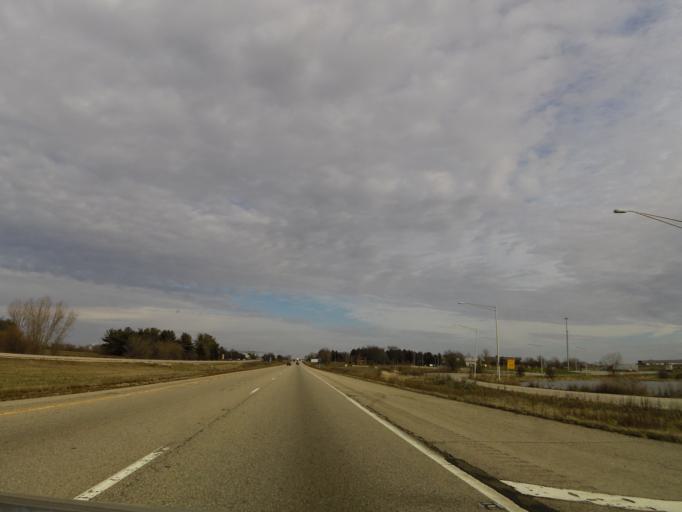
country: US
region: Wisconsin
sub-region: Rock County
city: Beloit
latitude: 42.5036
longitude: -88.9884
